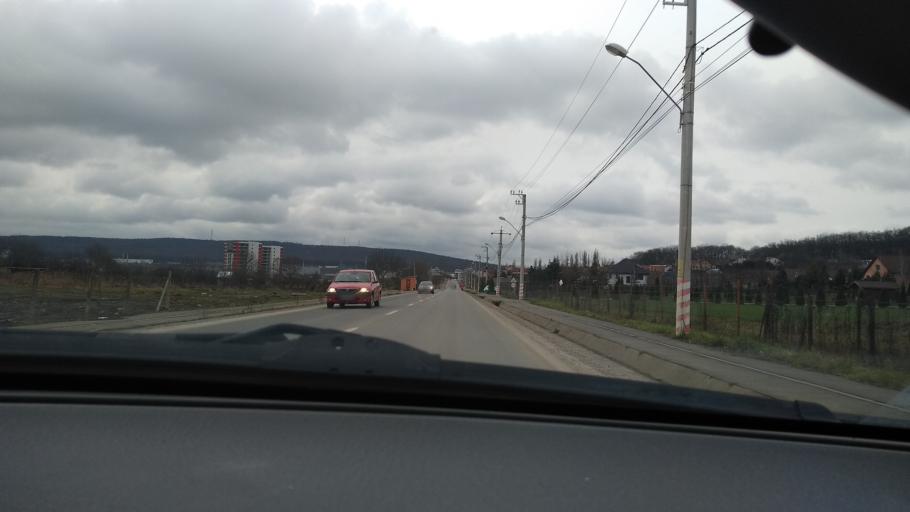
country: RO
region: Mures
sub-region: Comuna Corunca
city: Corunca
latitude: 46.5408
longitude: 24.6086
